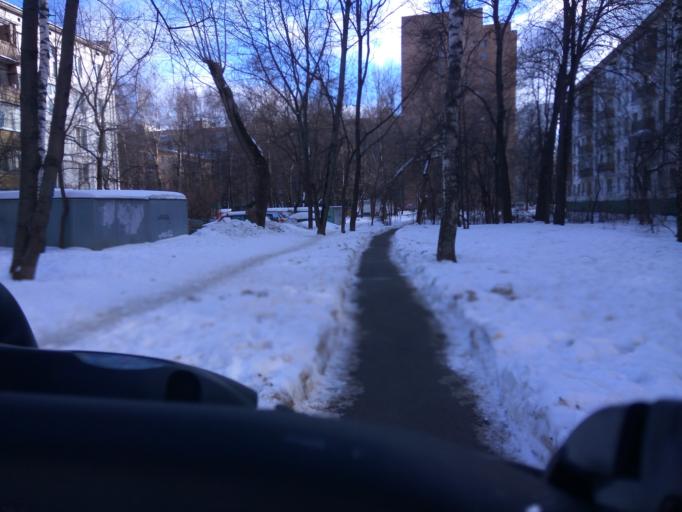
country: RU
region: Moskovskaya
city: Bogorodskoye
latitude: 55.7997
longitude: 37.7246
